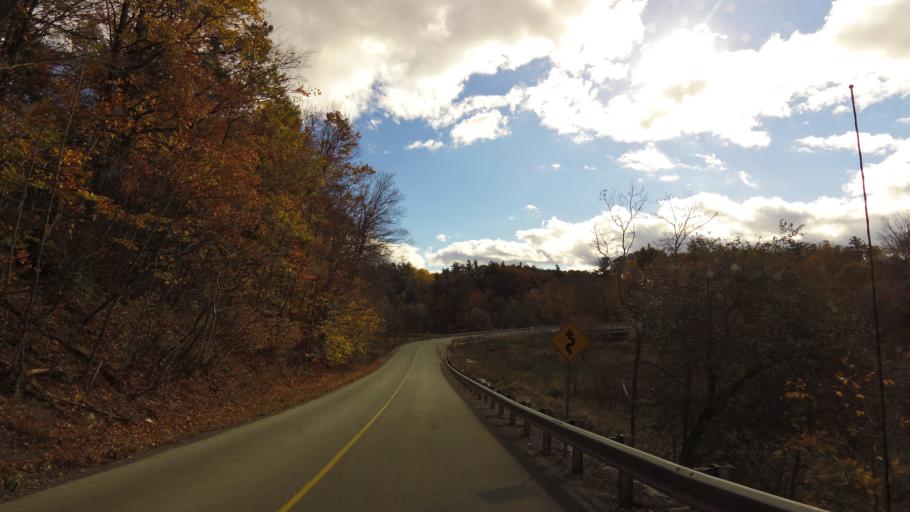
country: CA
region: Ontario
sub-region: Halton
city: Milton
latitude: 43.4756
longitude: -79.7977
